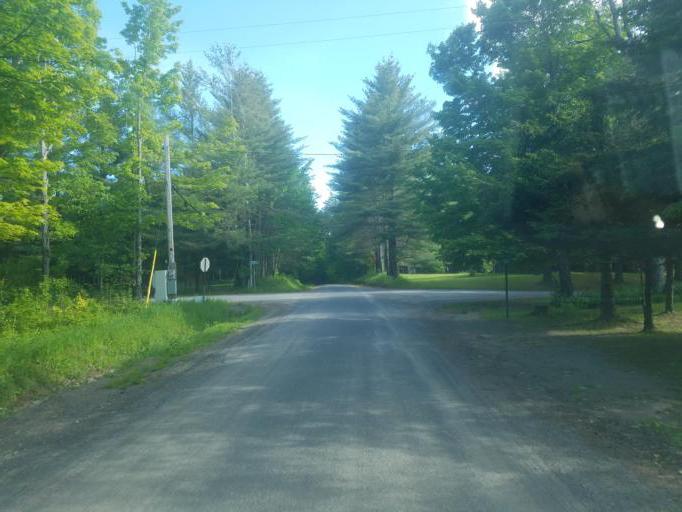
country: US
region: New York
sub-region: Herkimer County
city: Dolgeville
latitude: 43.3599
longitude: -74.9202
